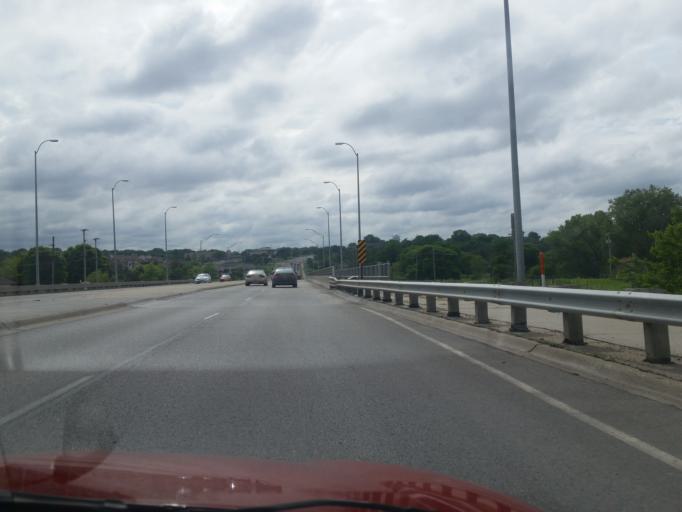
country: US
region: Nebraska
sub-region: Sarpy County
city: Offutt Air Force Base
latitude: 41.1180
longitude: -95.9366
